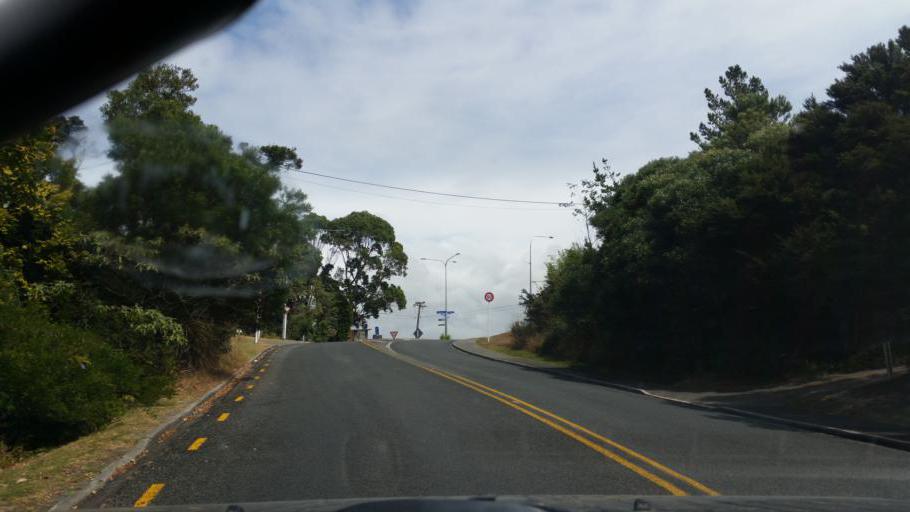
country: NZ
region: Auckland
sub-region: Auckland
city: Wellsford
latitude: -36.0869
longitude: 174.5835
